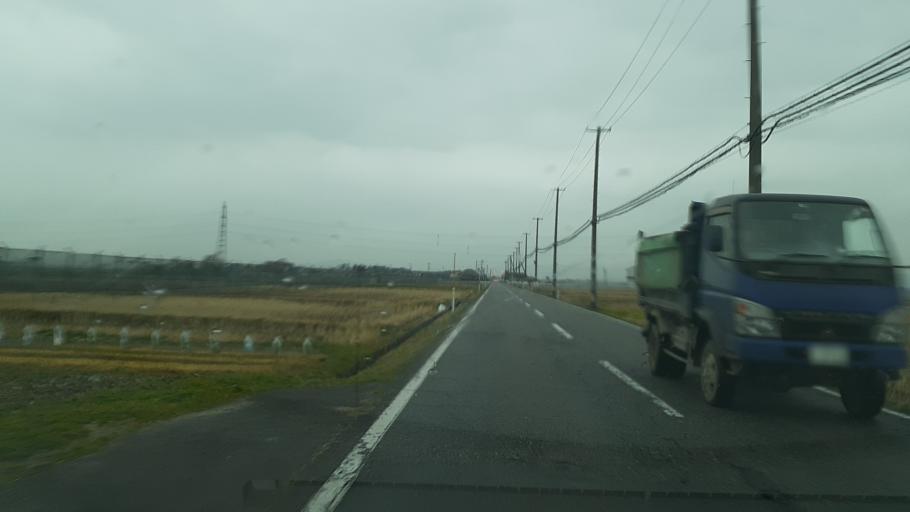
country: JP
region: Niigata
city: Suibara
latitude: 37.8862
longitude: 139.1817
